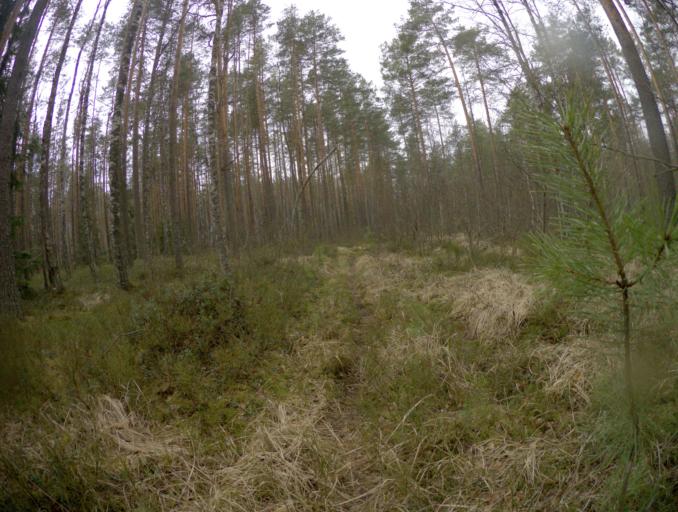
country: RU
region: Vladimir
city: Raduzhnyy
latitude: 55.9529
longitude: 40.2899
